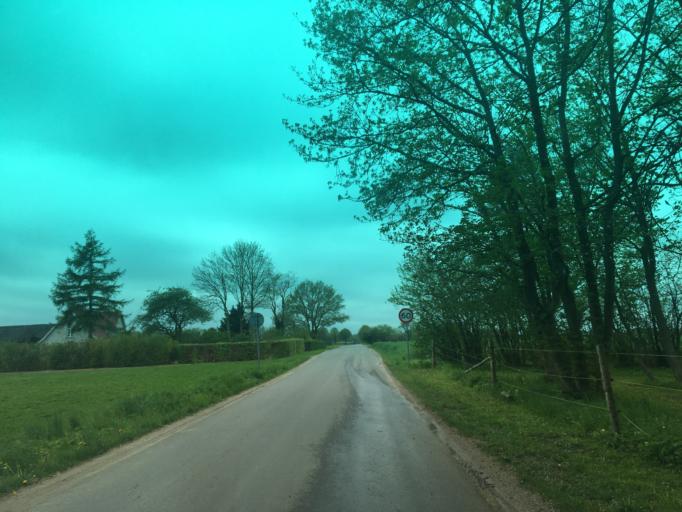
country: DK
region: Zealand
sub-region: Ringsted Kommune
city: Ringsted
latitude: 55.4094
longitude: 11.6904
